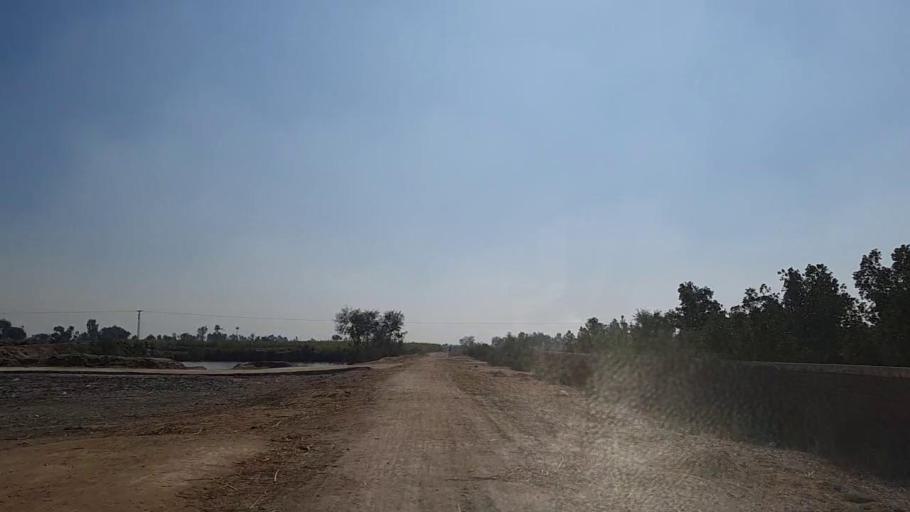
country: PK
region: Sindh
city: Bandhi
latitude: 26.5439
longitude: 68.3320
